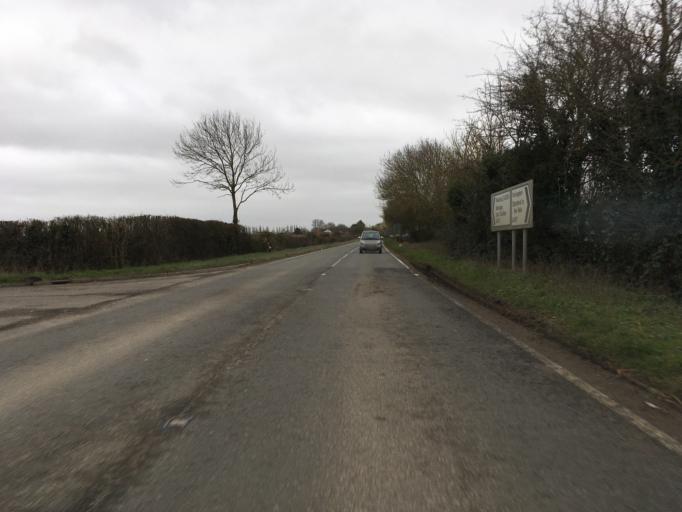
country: GB
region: England
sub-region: Oxfordshire
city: Stanford in the Vale
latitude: 51.6192
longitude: -1.4953
